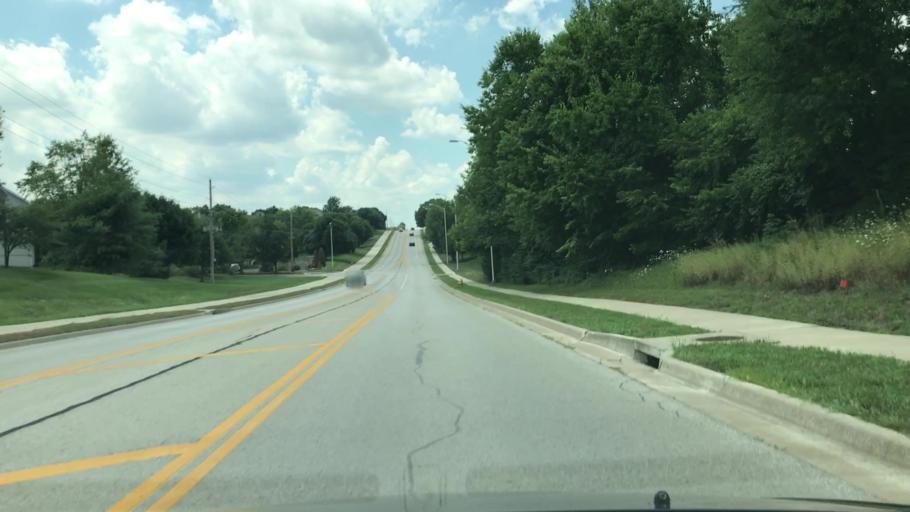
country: US
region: Missouri
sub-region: Jackson County
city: Lees Summit
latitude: 38.9050
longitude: -94.4270
